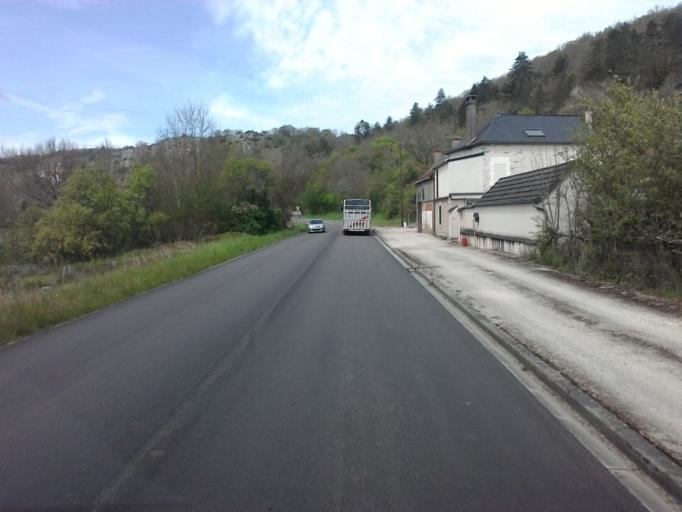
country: FR
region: Bourgogne
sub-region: Departement de l'Yonne
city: Joux-la-Ville
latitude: 47.5815
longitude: 3.7789
